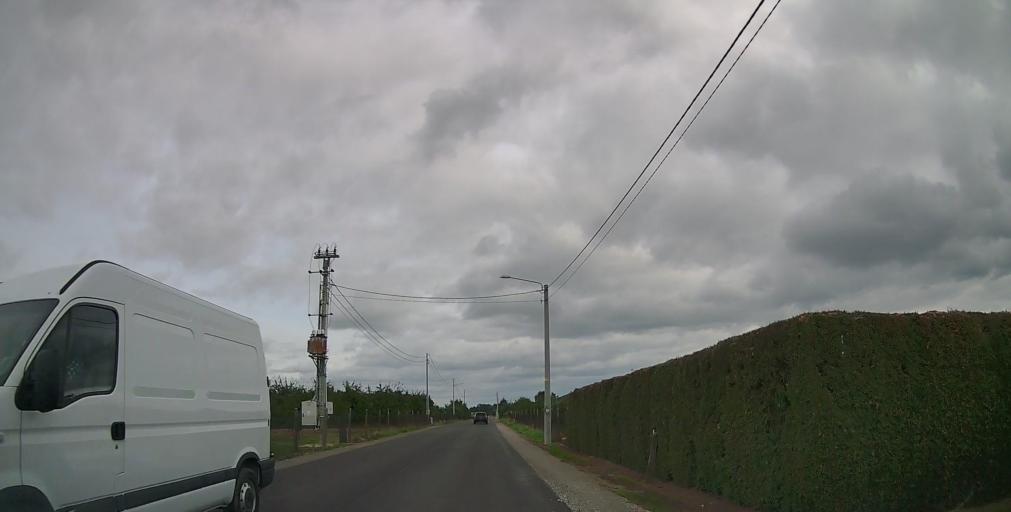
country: PL
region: Masovian Voivodeship
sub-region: Powiat grojecki
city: Belsk Duzy
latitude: 51.8111
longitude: 20.8375
